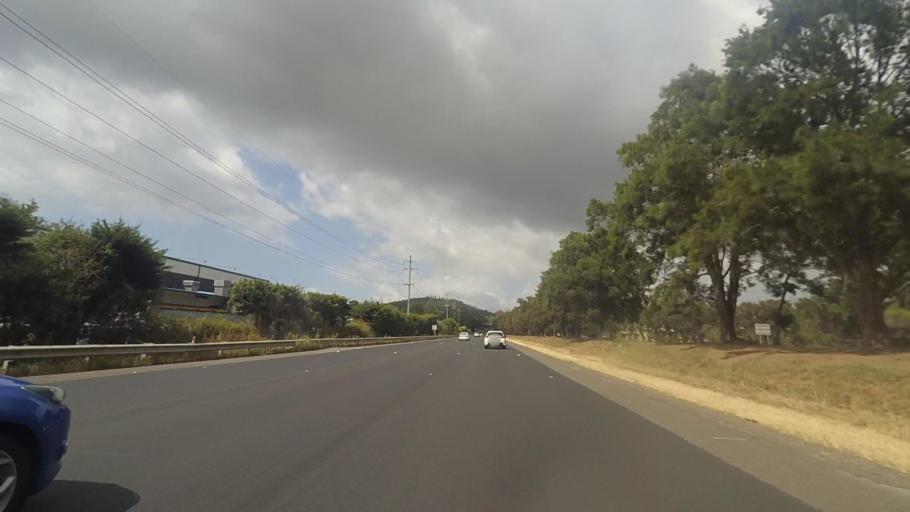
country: AU
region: New South Wales
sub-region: Wollongong
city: Mount Saint Thomas
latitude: -34.4579
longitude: 150.8555
